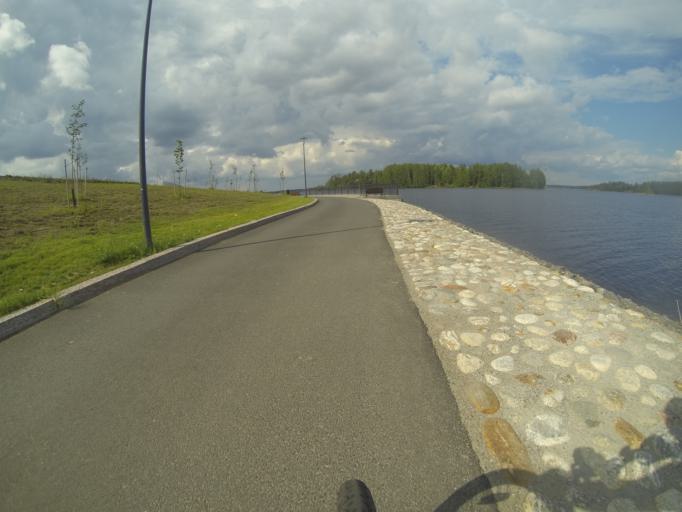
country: FI
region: Southern Savonia
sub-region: Savonlinna
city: Savonlinna
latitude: 61.8734
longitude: 28.8816
